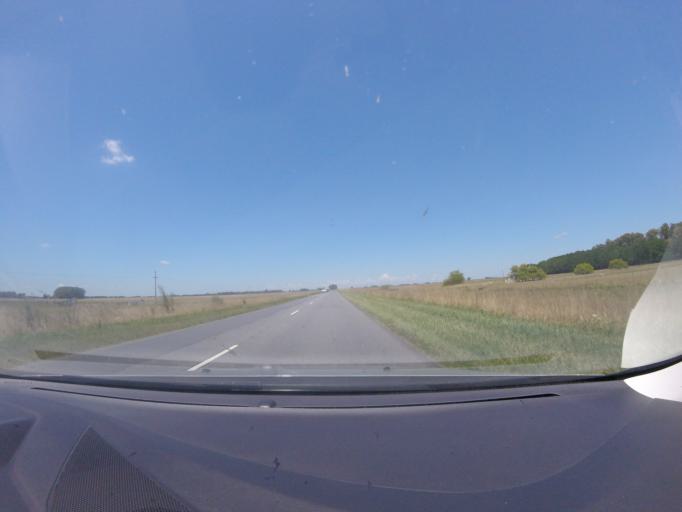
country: AR
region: Buenos Aires
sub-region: Partido de Rauch
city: Rauch
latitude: -36.6301
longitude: -59.0640
